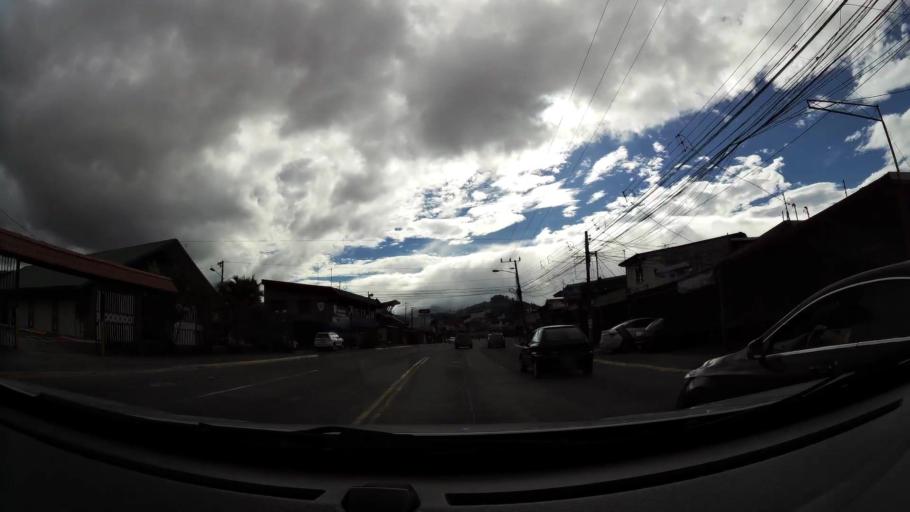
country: CR
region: San Jose
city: San Pedro
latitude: 9.9093
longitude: -84.0539
